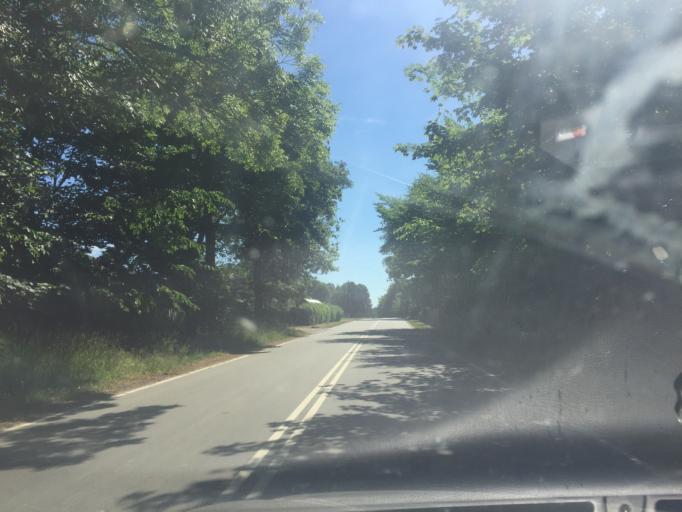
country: DK
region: Capital Region
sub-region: Hoje-Taastrup Kommune
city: Flong
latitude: 55.6676
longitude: 12.2268
